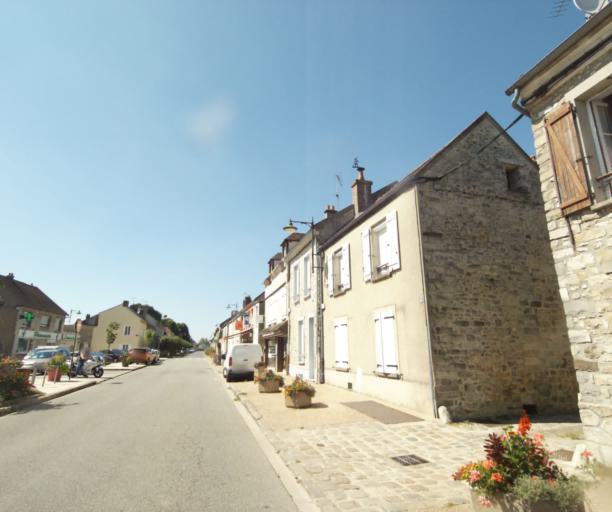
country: FR
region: Ile-de-France
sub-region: Departement de Seine-et-Marne
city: La Chapelle-la-Reine
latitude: 48.3178
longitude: 2.5700
